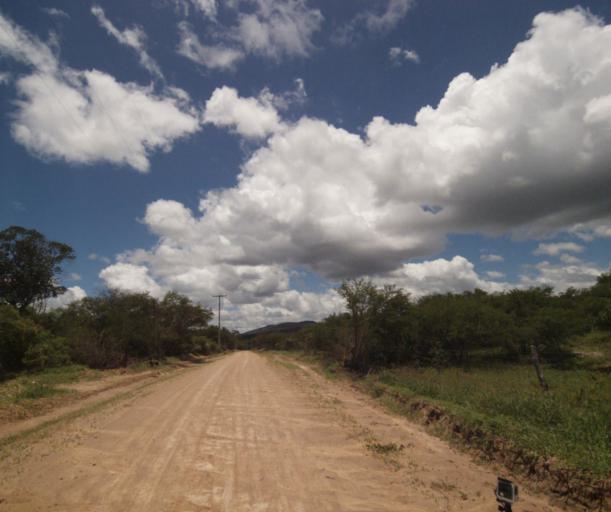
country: BR
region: Bahia
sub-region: Pocoes
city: Pocoes
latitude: -14.3821
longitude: -40.3854
